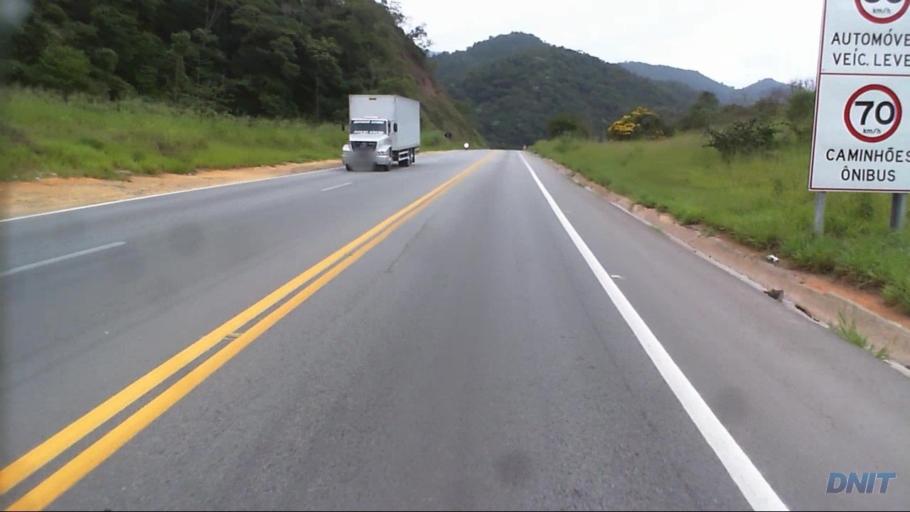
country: BR
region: Minas Gerais
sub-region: Nova Era
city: Nova Era
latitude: -19.6436
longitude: -42.9121
